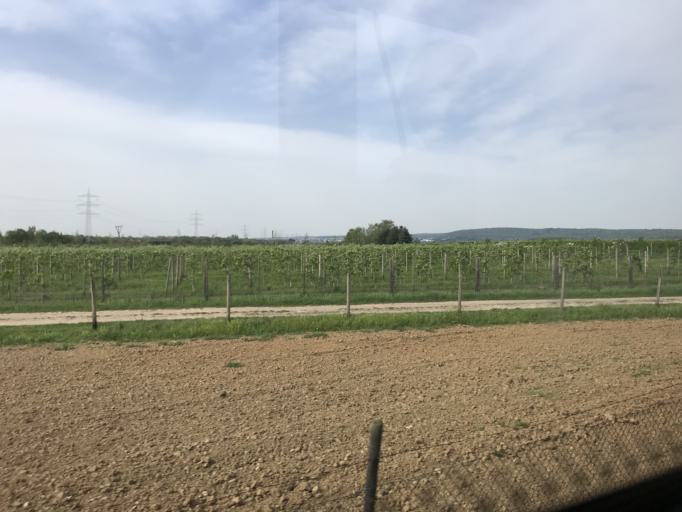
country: DE
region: Hesse
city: Sulzbach
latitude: 50.1128
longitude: 8.5166
